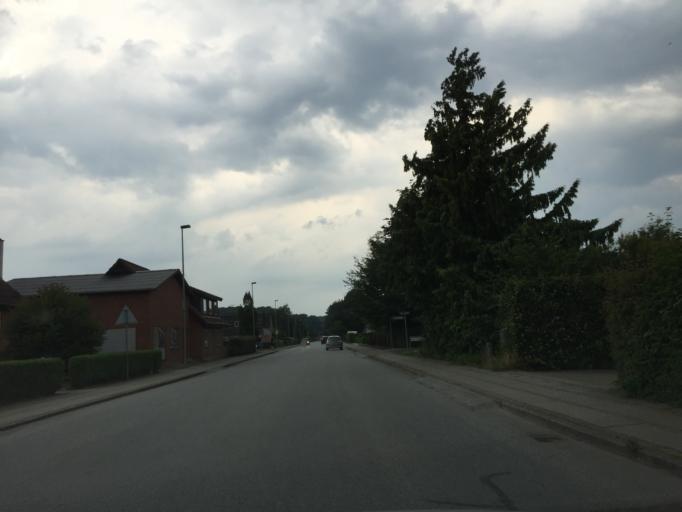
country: DK
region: Central Jutland
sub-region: Viborg Kommune
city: Bjerringbro
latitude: 56.3098
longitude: 9.5884
